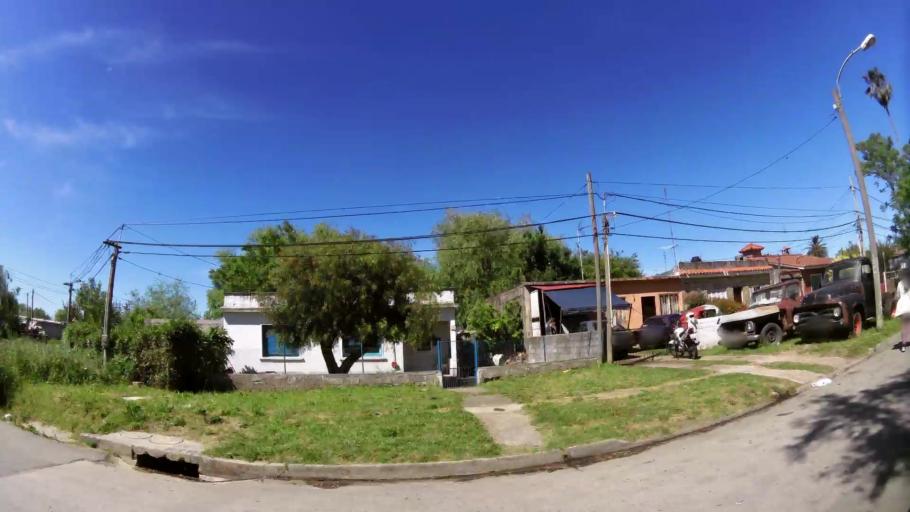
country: UY
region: Canelones
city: Paso de Carrasco
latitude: -34.8553
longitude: -56.1143
